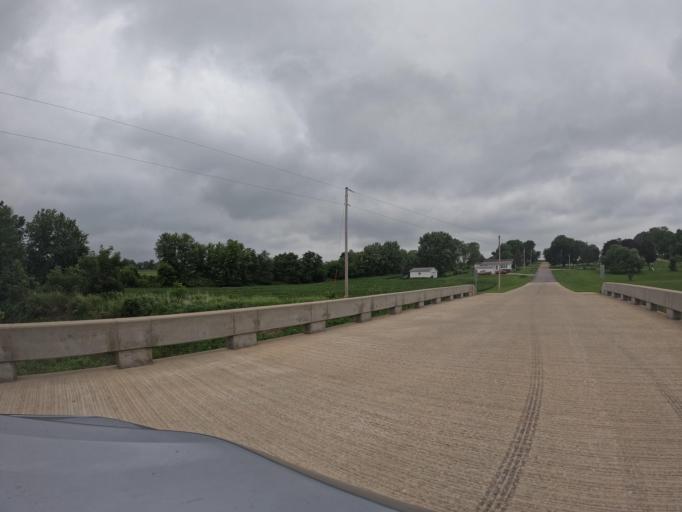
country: US
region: Iowa
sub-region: Clinton County
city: De Witt
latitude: 41.9128
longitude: -90.5996
